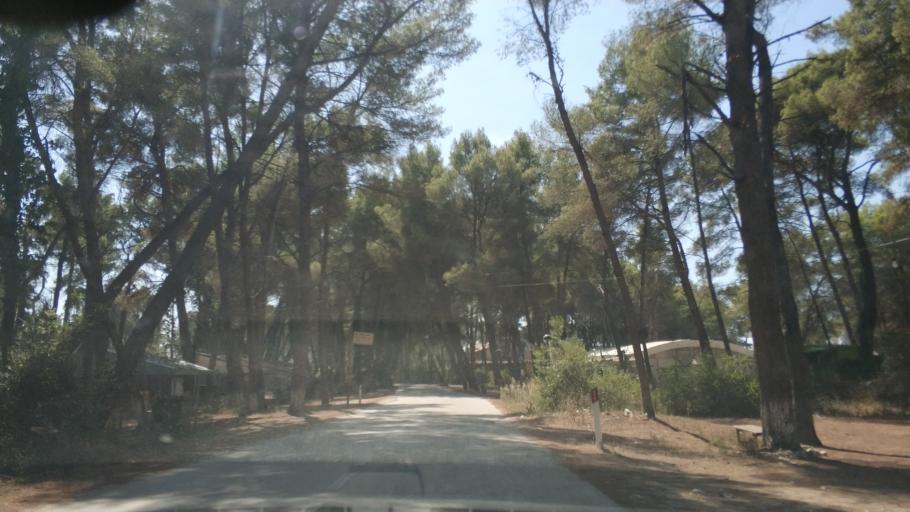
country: AL
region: Fier
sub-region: Rrethi i Lushnjes
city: Divjake
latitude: 40.9752
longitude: 19.4809
